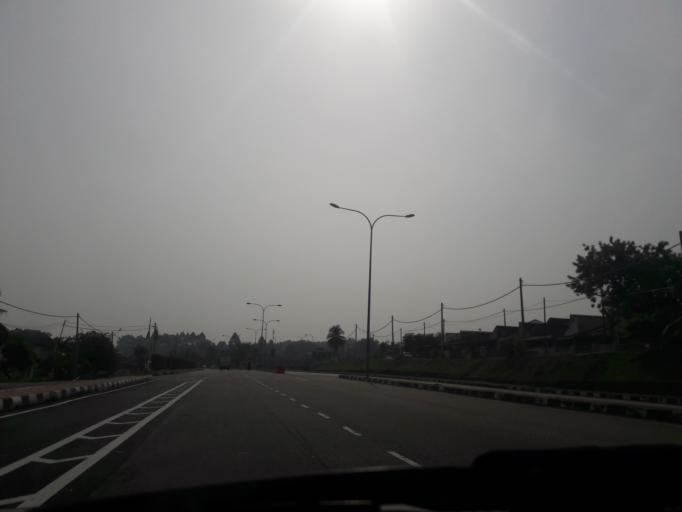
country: MY
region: Kedah
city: Kulim
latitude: 5.3563
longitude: 100.5404
